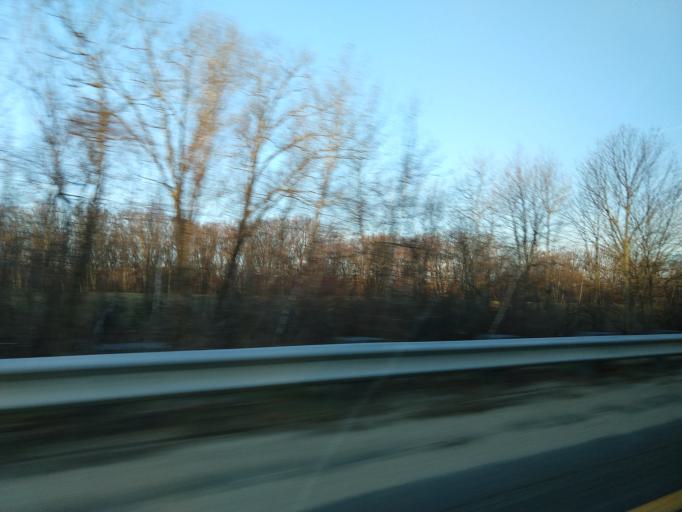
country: US
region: Massachusetts
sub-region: Essex County
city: South Peabody
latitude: 42.5296
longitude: -70.9780
